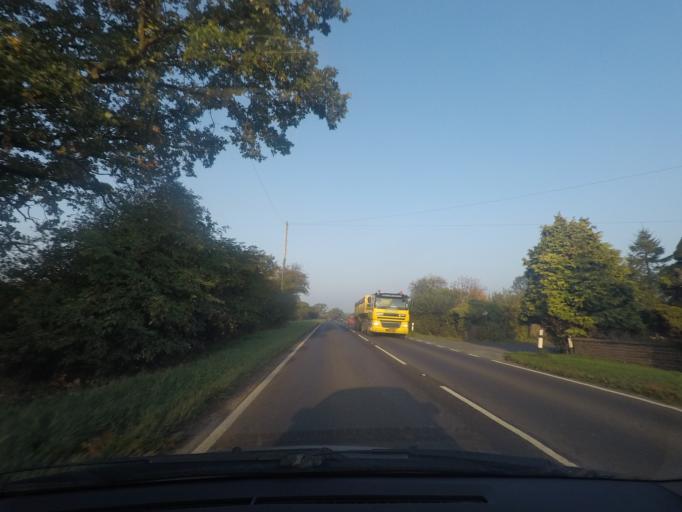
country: GB
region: England
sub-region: City of York
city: Askham Richard
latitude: 53.9933
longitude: -1.2428
